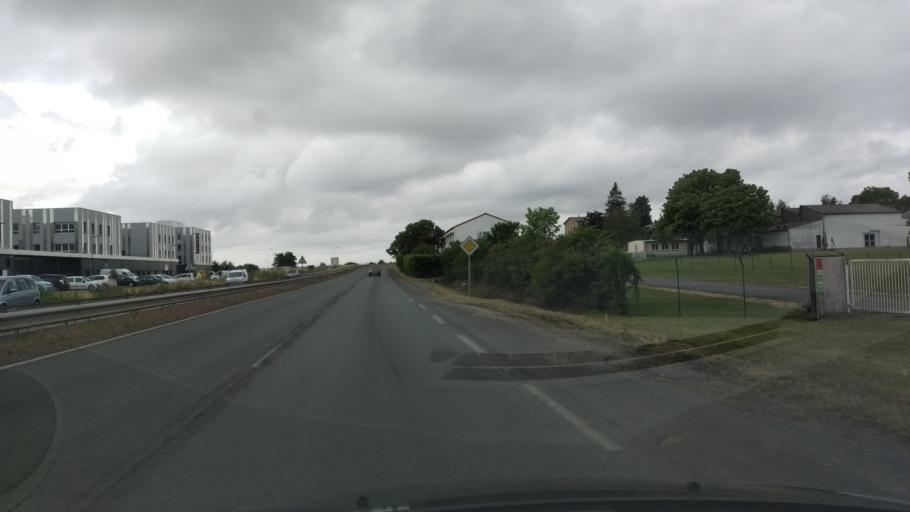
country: FR
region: Poitou-Charentes
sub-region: Departement de la Vienne
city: Biard
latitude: 46.5851
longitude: 0.3144
